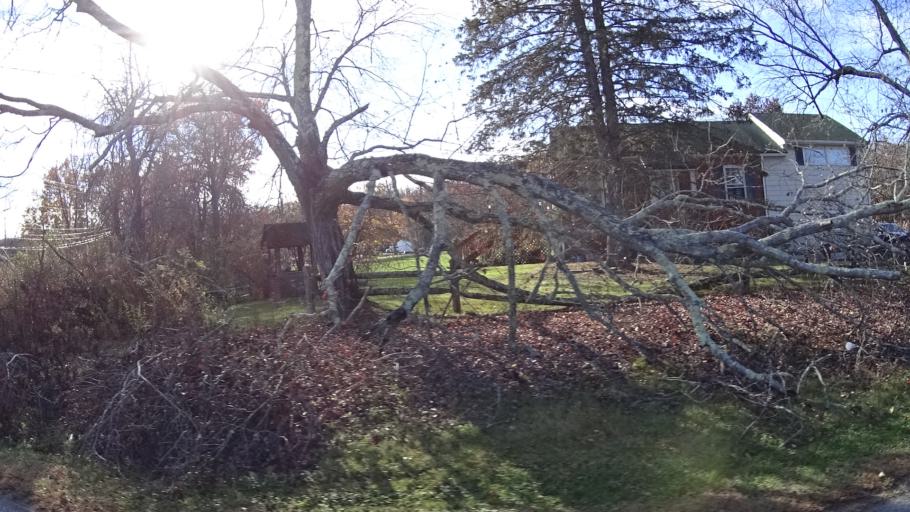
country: US
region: New Jersey
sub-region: Union County
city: Berkeley Heights
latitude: 40.6940
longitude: -74.4720
